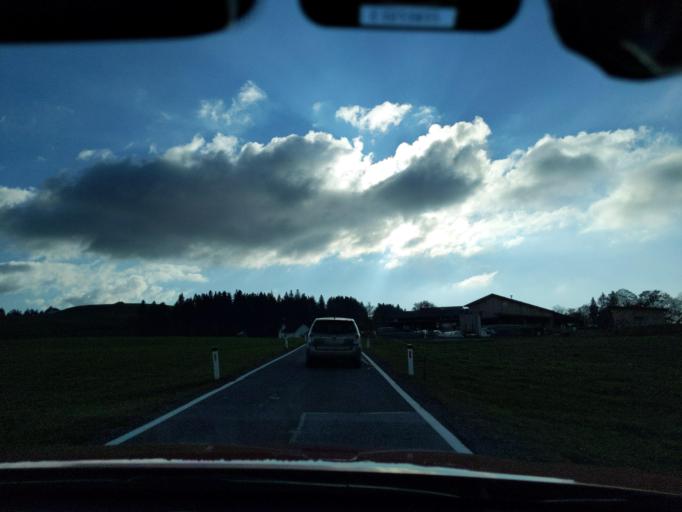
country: AT
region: Vorarlberg
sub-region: Politischer Bezirk Bregenz
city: Moggers
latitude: 47.5648
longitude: 9.7969
